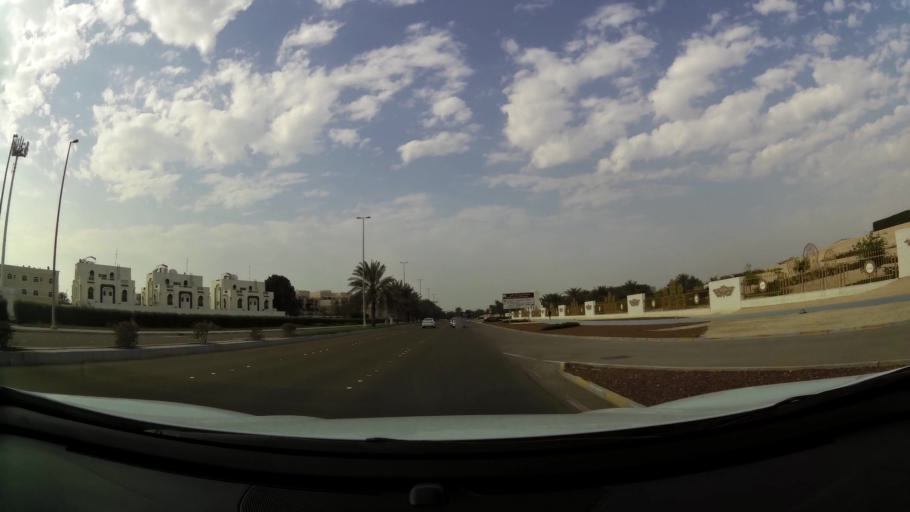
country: AE
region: Abu Dhabi
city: Abu Dhabi
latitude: 24.4140
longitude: 54.4723
